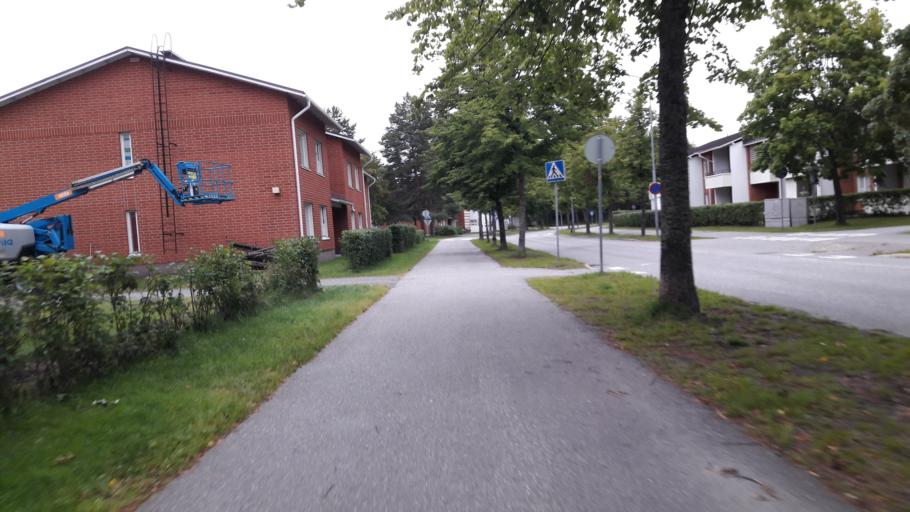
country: FI
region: North Karelia
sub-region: Joensuu
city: Joensuu
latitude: 62.6175
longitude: 29.7090
